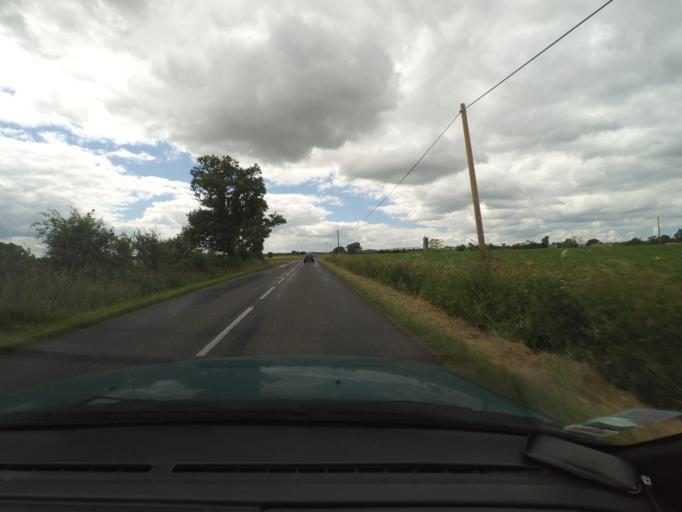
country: FR
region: Pays de la Loire
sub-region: Departement de la Loire-Atlantique
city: Saint-Hilaire-de-Clisson
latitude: 47.0494
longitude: -1.3214
